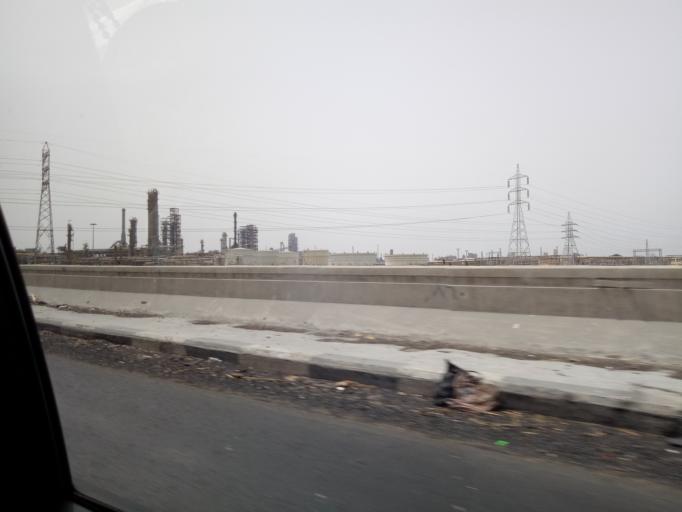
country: EG
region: Alexandria
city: Alexandria
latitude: 31.1363
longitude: 29.8548
